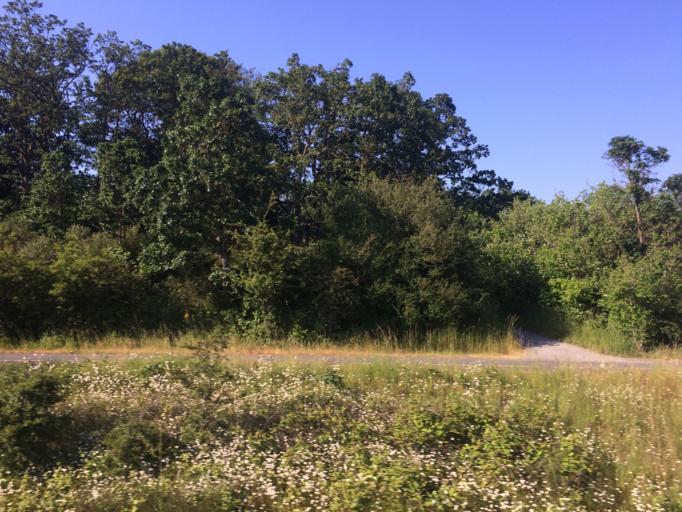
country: CA
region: British Columbia
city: Victoria
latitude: 48.4602
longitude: -123.4071
